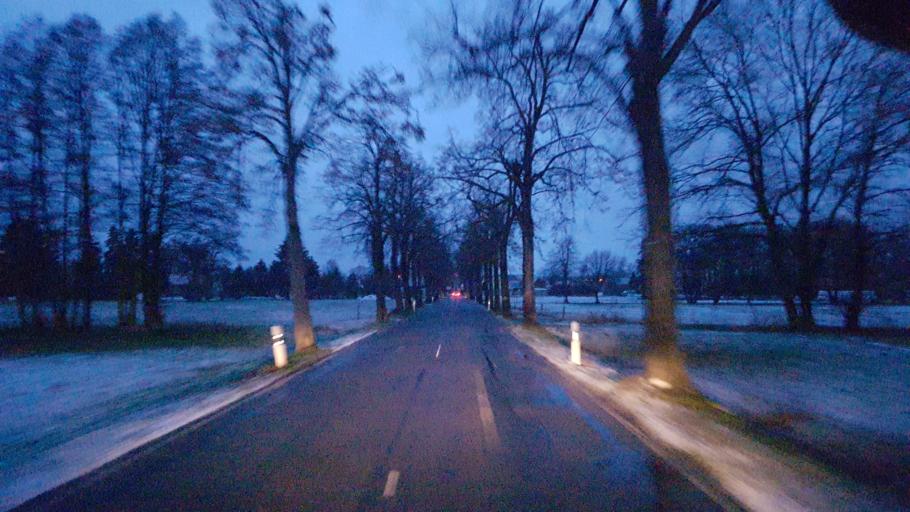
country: DE
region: Brandenburg
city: Werben
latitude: 51.7754
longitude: 14.1974
